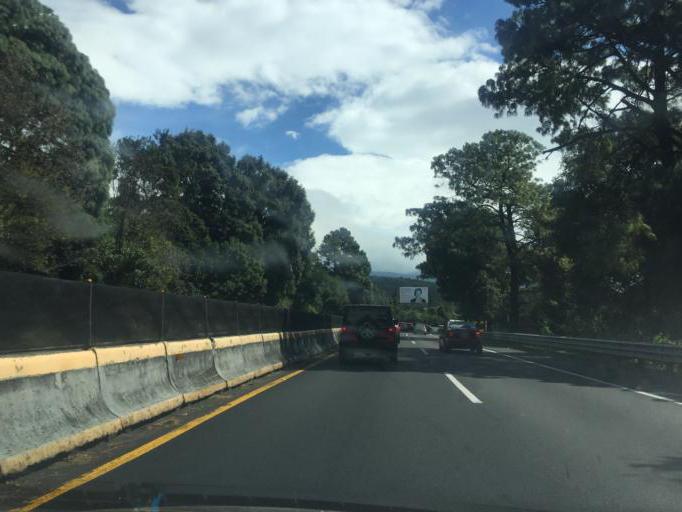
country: MX
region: Morelos
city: Tres Marias
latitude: 19.0314
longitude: -99.2113
